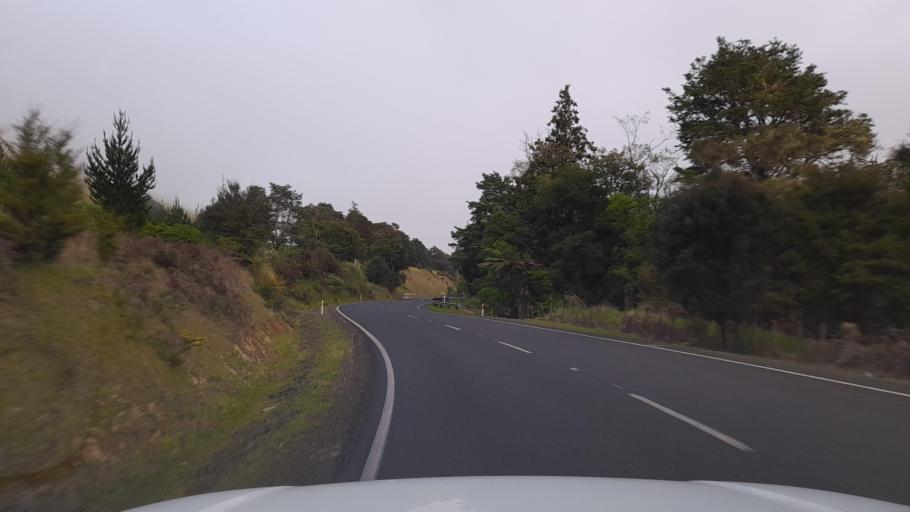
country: NZ
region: Northland
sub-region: Kaipara District
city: Dargaville
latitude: -35.6304
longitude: 173.8541
